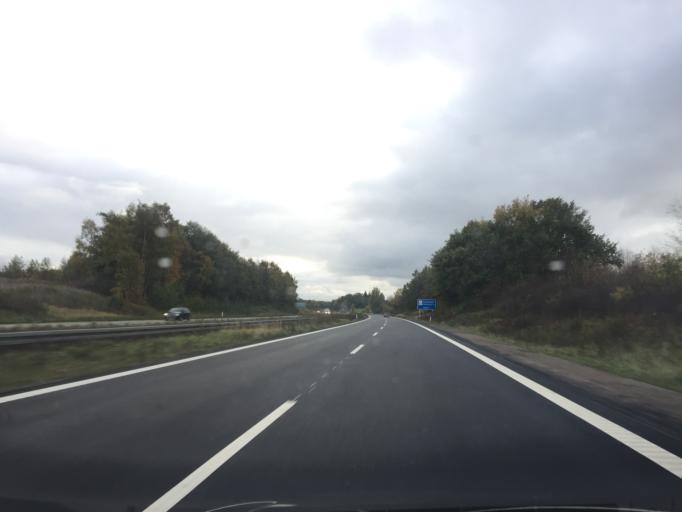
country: DK
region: Capital Region
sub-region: Fredensborg Kommune
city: Kokkedal
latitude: 55.9185
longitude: 12.4727
